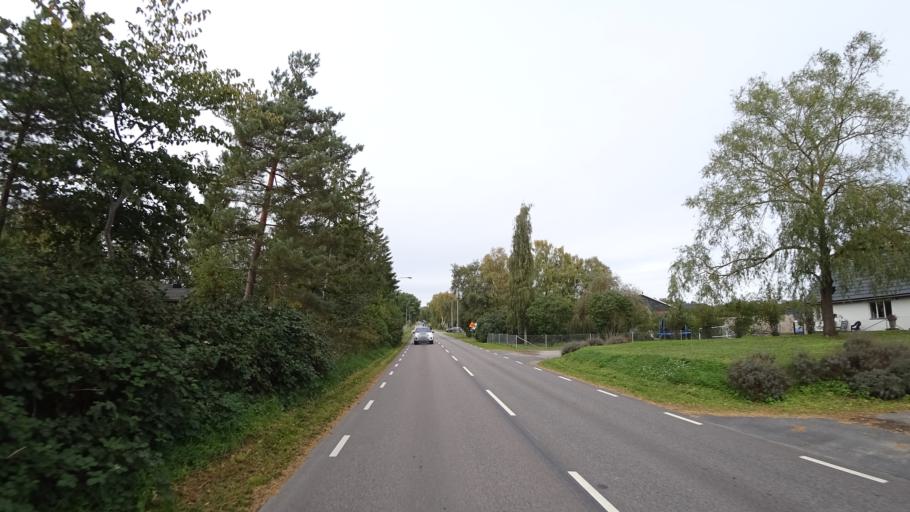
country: SE
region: Skane
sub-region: Kavlinge Kommun
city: Hofterup
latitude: 55.8020
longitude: 12.9866
